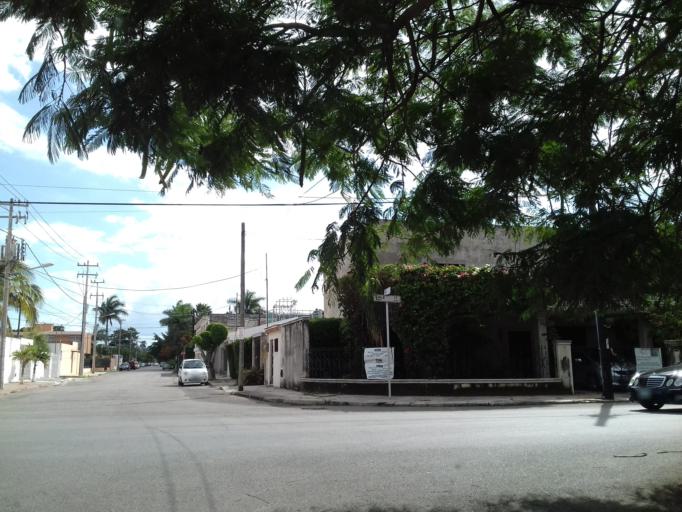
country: MX
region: Yucatan
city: Merida
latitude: 21.0038
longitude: -89.6085
